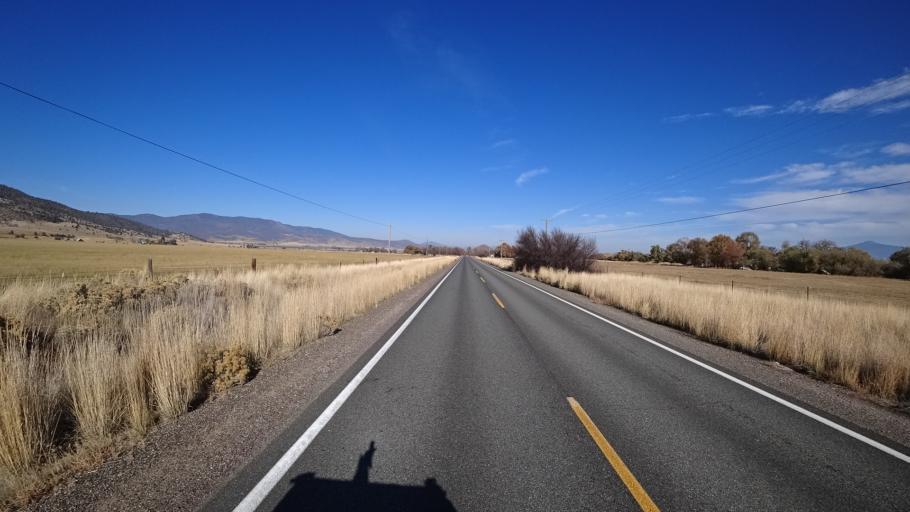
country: US
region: California
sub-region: Siskiyou County
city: Weed
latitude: 41.5098
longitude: -122.5175
